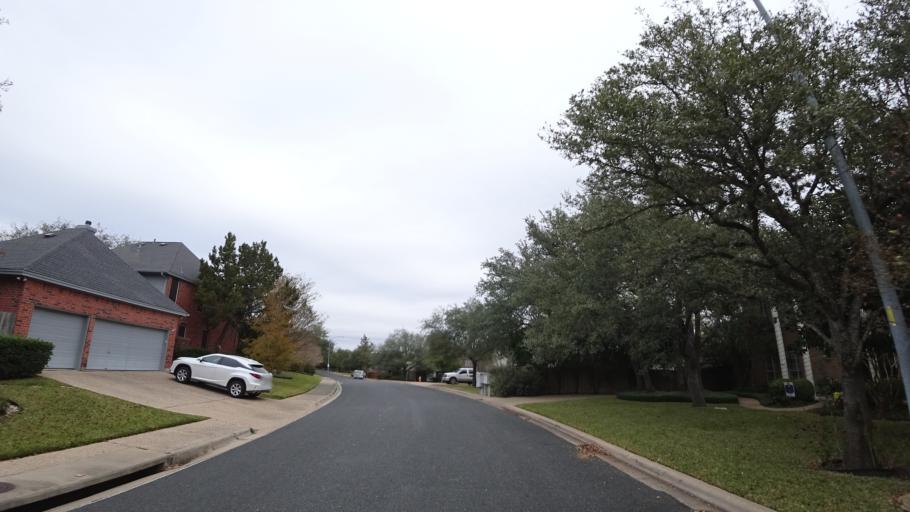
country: US
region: Texas
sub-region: Williamson County
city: Jollyville
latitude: 30.3810
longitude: -97.7971
